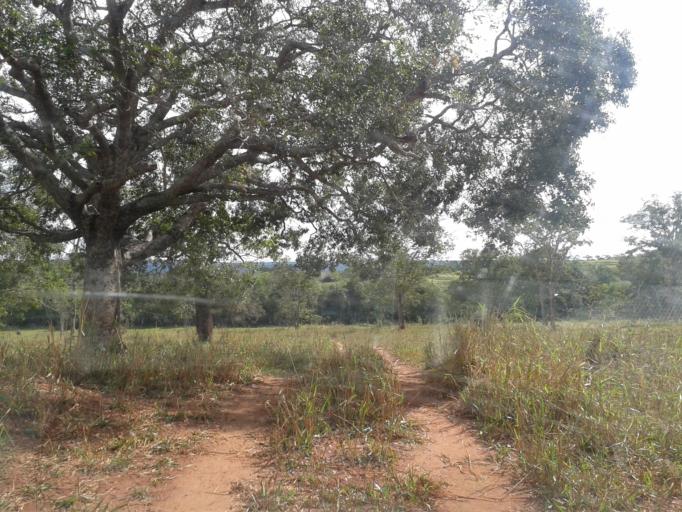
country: BR
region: Minas Gerais
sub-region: Campina Verde
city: Campina Verde
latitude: -19.4265
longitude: -49.7120
